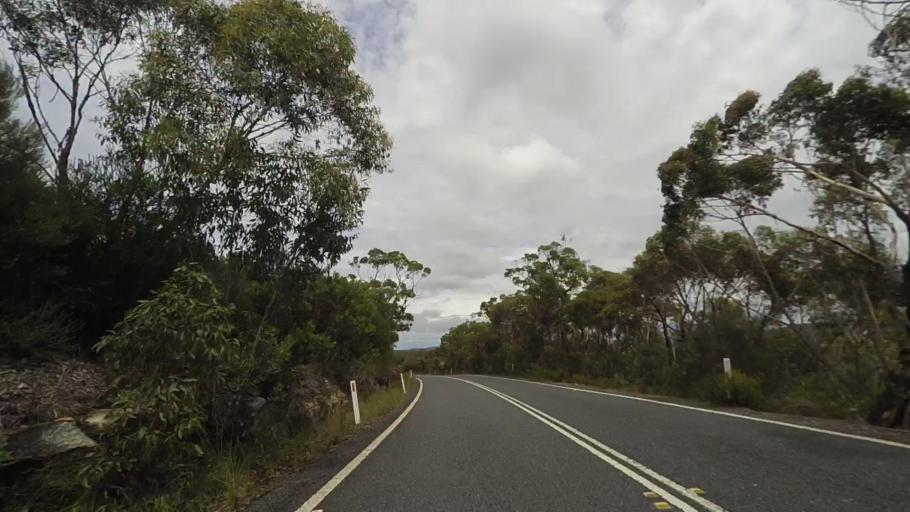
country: AU
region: New South Wales
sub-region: Sutherland Shire
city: Heathcote
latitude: -34.1079
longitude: 151.0602
